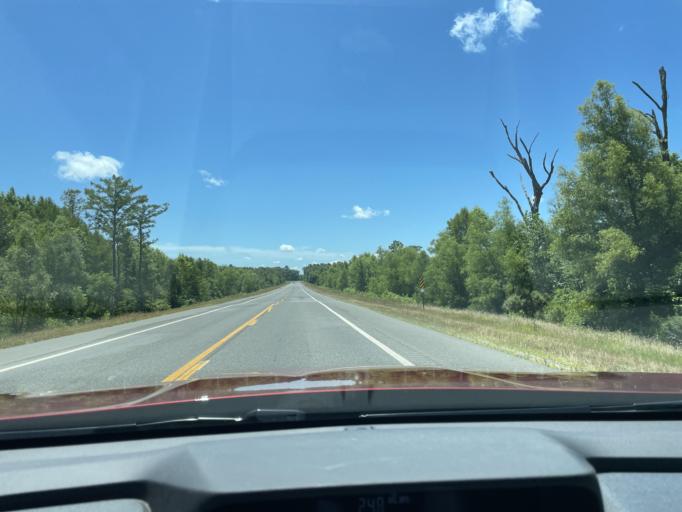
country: US
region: Arkansas
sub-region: Jefferson County
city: Pine Bluff
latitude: 34.1265
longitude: -91.9712
